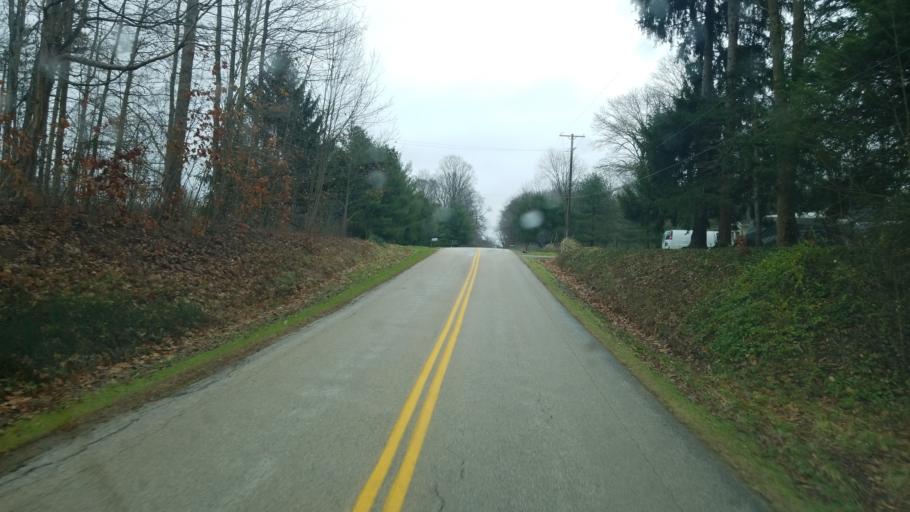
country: US
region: Ohio
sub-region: Ashtabula County
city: Roaming Shores
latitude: 41.7097
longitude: -80.8605
